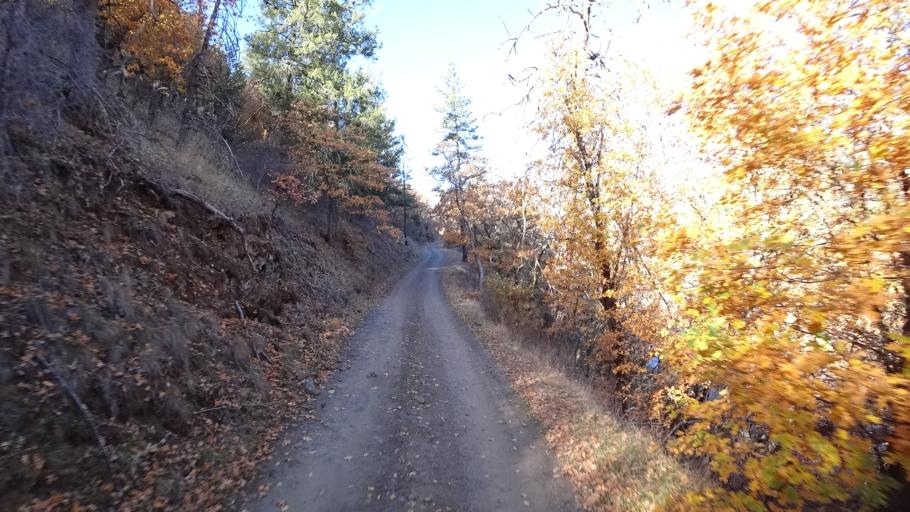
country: US
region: California
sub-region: Siskiyou County
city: Yreka
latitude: 41.8666
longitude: -122.8102
